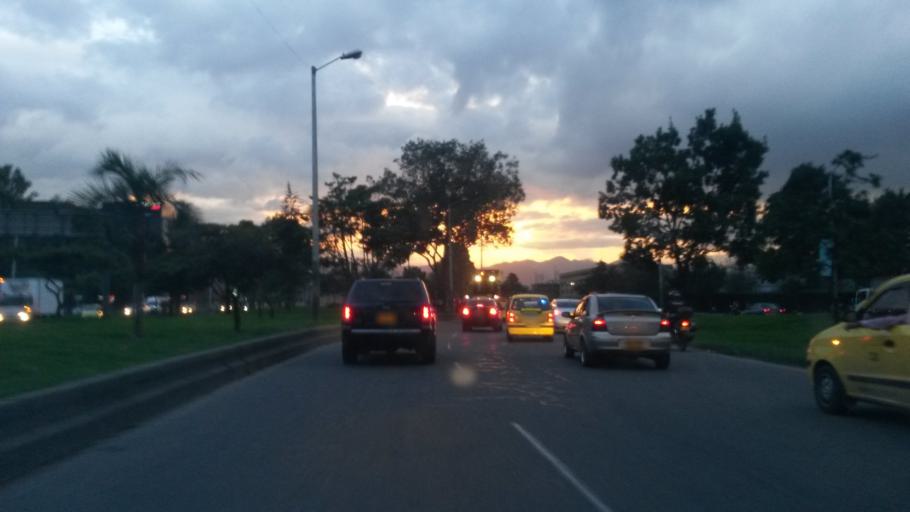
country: CO
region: Cundinamarca
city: Funza
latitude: 4.6884
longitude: -74.1296
